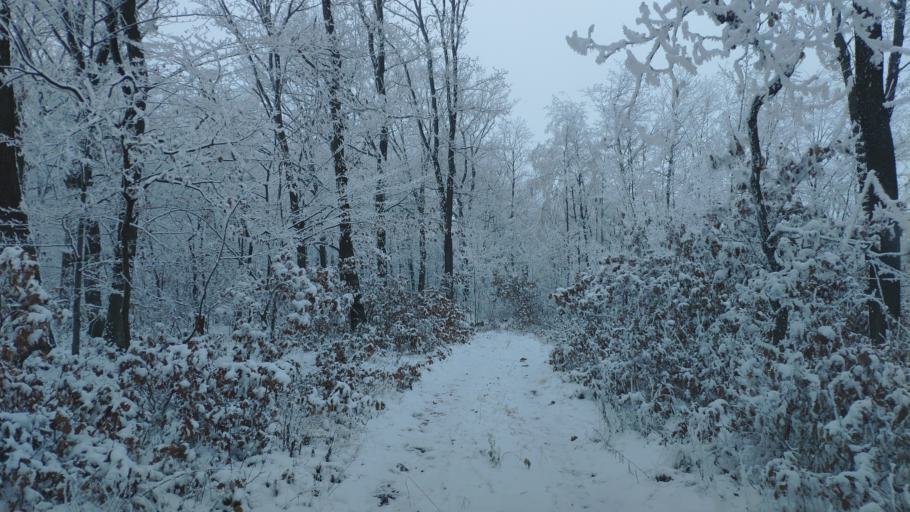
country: SK
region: Kosicky
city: Kosice
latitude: 48.6546
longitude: 21.1836
